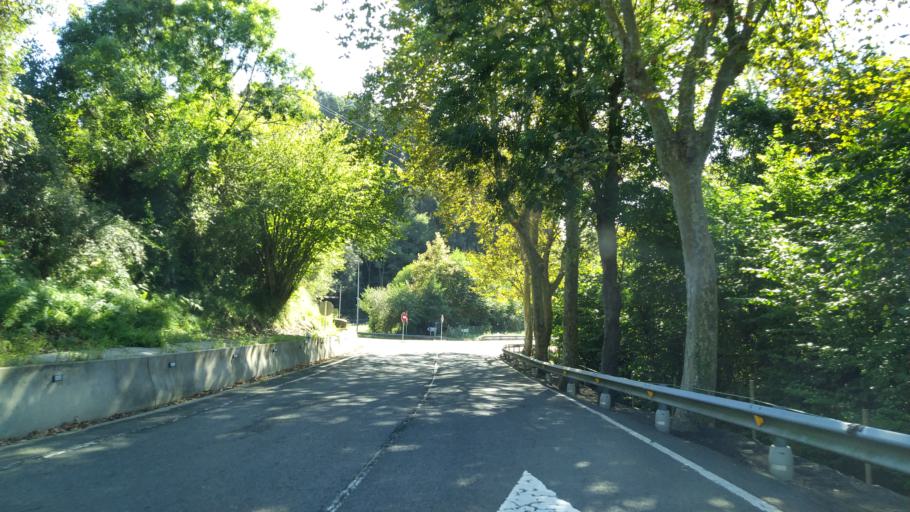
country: ES
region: Cantabria
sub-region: Provincia de Cantabria
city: Liendo
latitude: 43.3902
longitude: -3.3162
